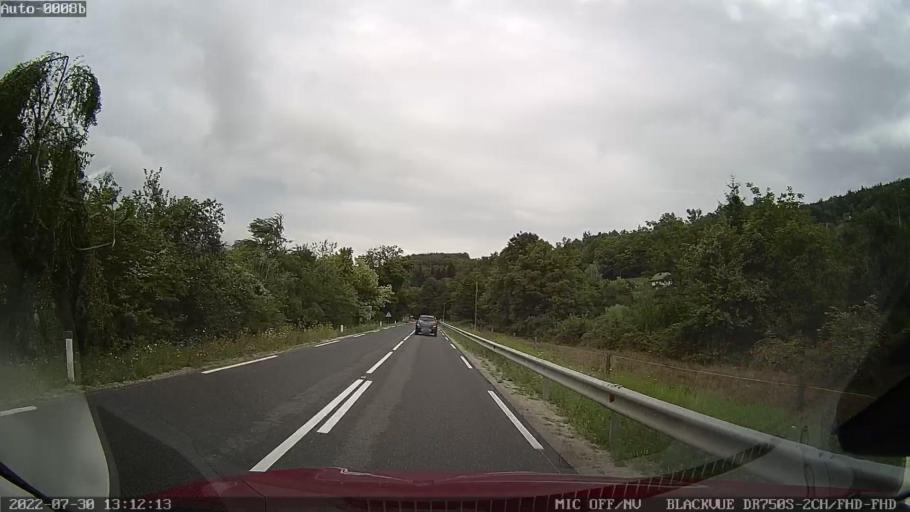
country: SI
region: Dolenjske Toplice
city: Dolenjske Toplice
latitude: 45.7100
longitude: 15.0722
